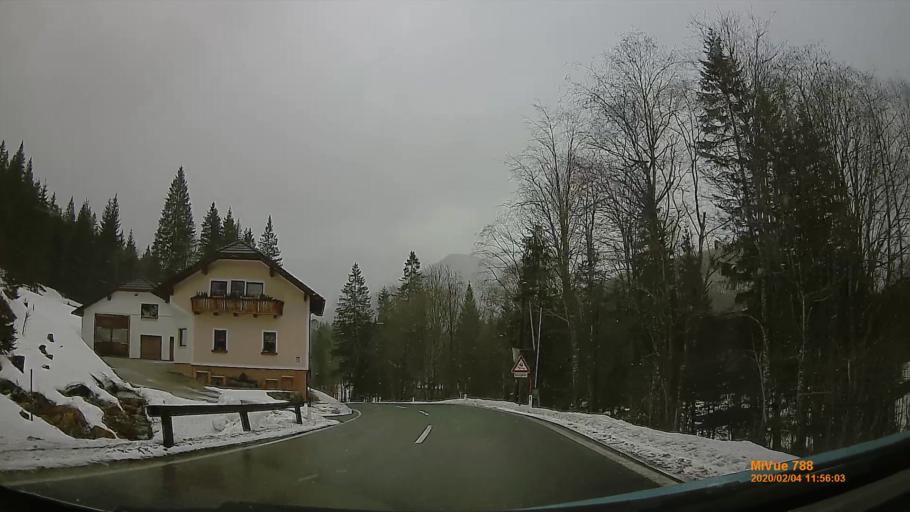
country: AT
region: Styria
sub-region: Politischer Bezirk Bruck-Muerzzuschlag
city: Muerzsteg
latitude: 47.7590
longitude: 15.5154
